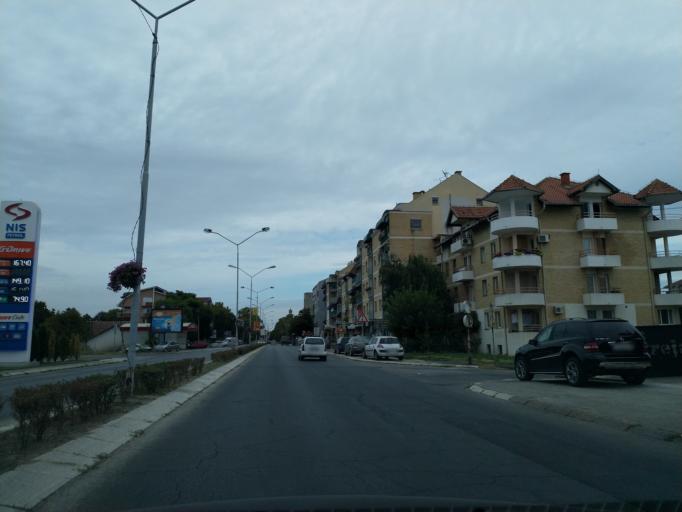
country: RS
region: Central Serbia
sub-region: Pomoravski Okrug
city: Jagodina
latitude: 43.9694
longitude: 21.2717
